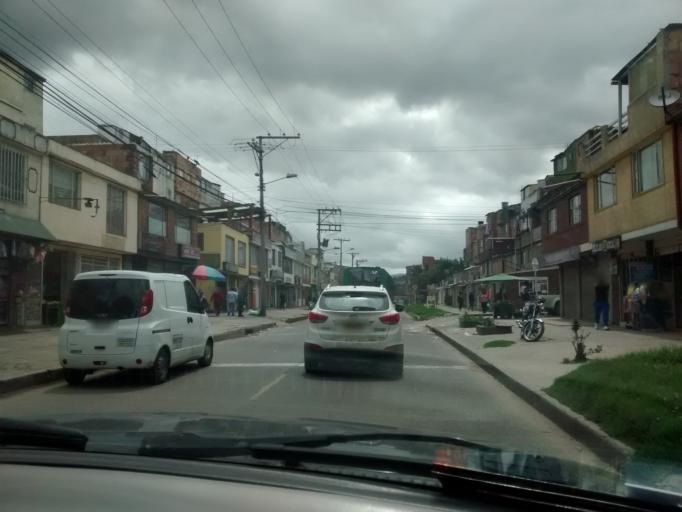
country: CO
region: Cundinamarca
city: Cota
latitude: 4.7164
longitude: -74.1042
